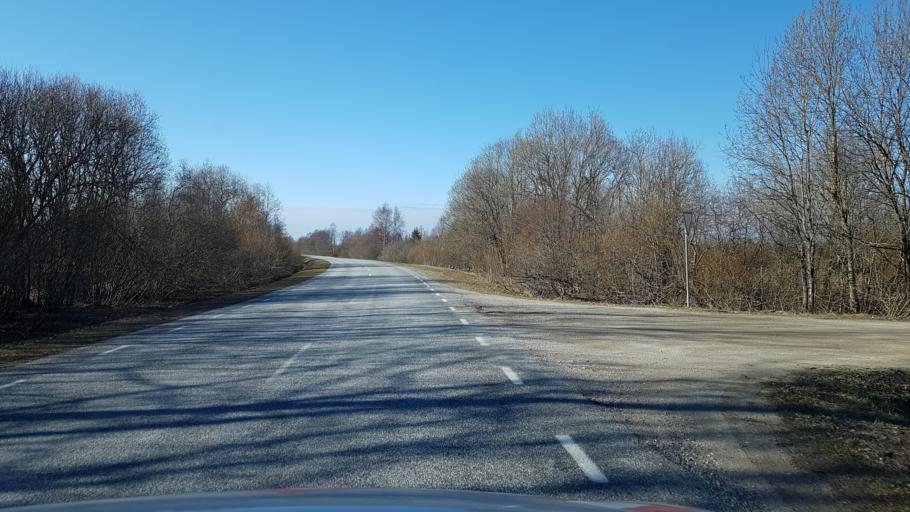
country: EE
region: Laeaene-Virumaa
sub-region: Haljala vald
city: Haljala
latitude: 59.4945
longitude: 26.1419
